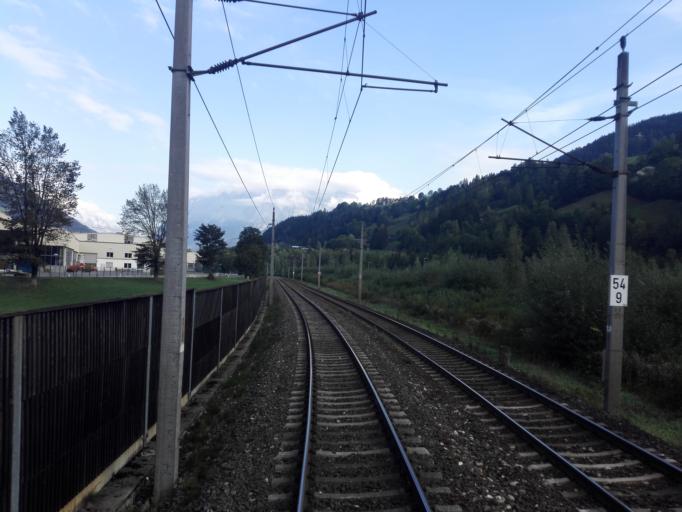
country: AT
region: Salzburg
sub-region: Politischer Bezirk Sankt Johann im Pongau
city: Bischofshofen
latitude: 47.3978
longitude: 13.2250
